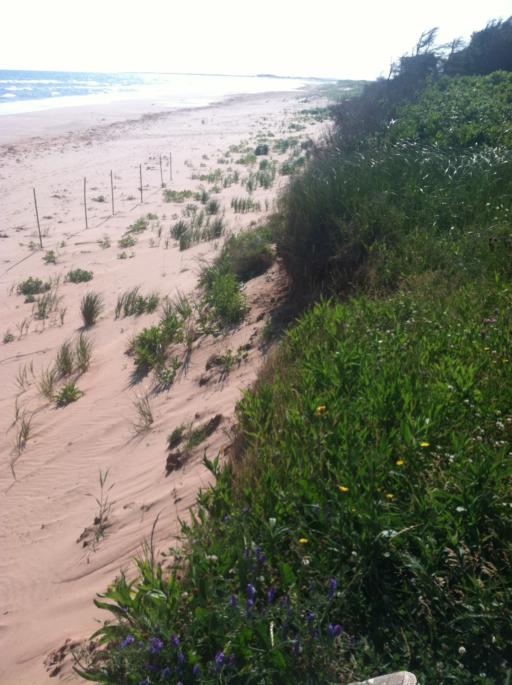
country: CA
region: Prince Edward Island
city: Charlottetown
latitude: 46.4172
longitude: -63.0739
